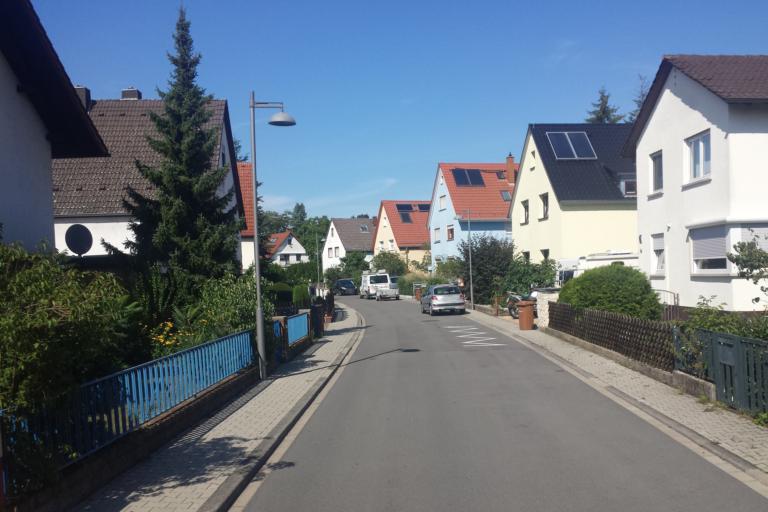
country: DE
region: Baden-Wuerttemberg
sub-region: Karlsruhe Region
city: Mannheim
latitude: 49.5294
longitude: 8.5033
